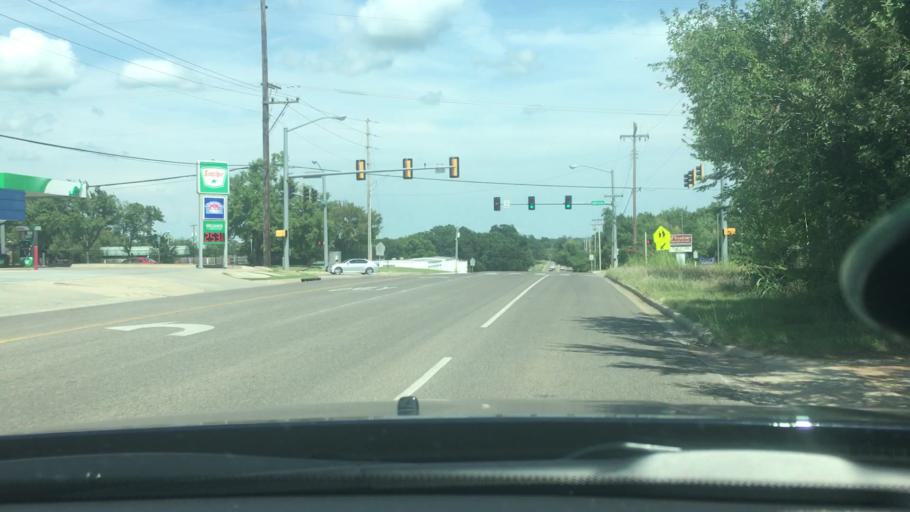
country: US
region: Oklahoma
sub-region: Pottawatomie County
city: Shawnee
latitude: 35.3326
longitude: -96.8952
